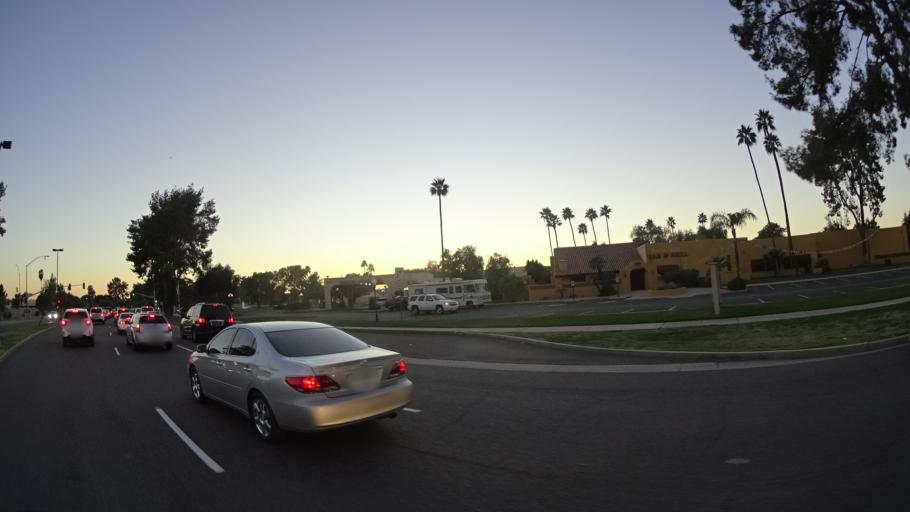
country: US
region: Arizona
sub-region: Maricopa County
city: San Carlos
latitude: 33.3838
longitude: -111.8749
